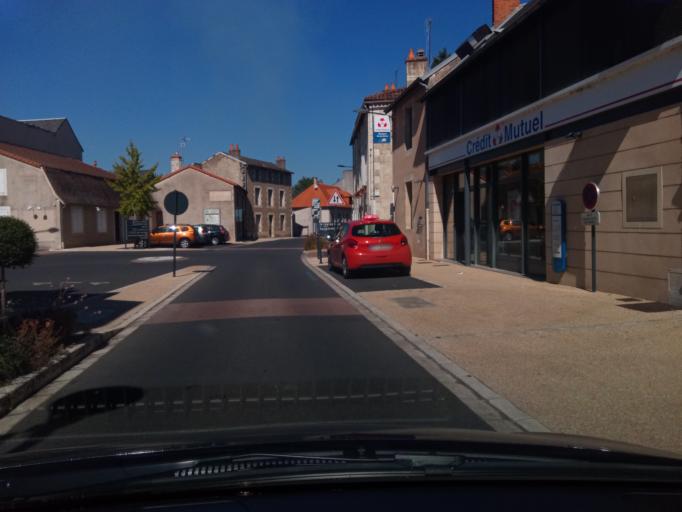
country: FR
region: Poitou-Charentes
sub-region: Departement de la Vienne
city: Montmorillon
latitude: 46.4269
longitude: 0.8694
